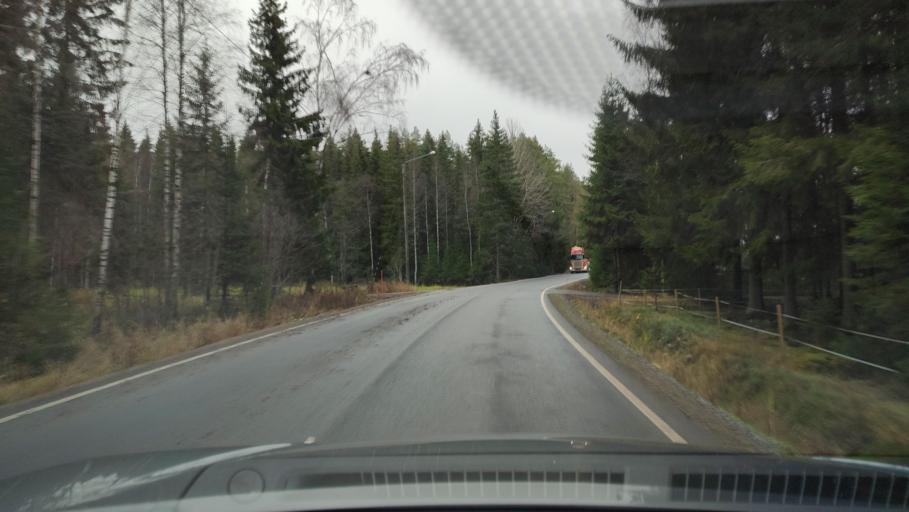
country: FI
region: Southern Ostrobothnia
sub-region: Suupohja
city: Karijoki
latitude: 62.1453
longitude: 21.6905
